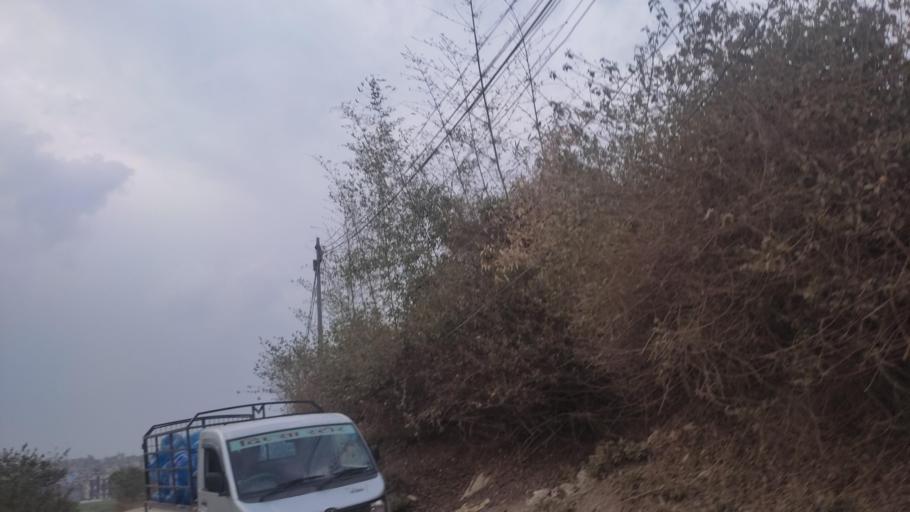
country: NP
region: Central Region
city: Kirtipur
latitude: 27.6641
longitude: 85.2874
